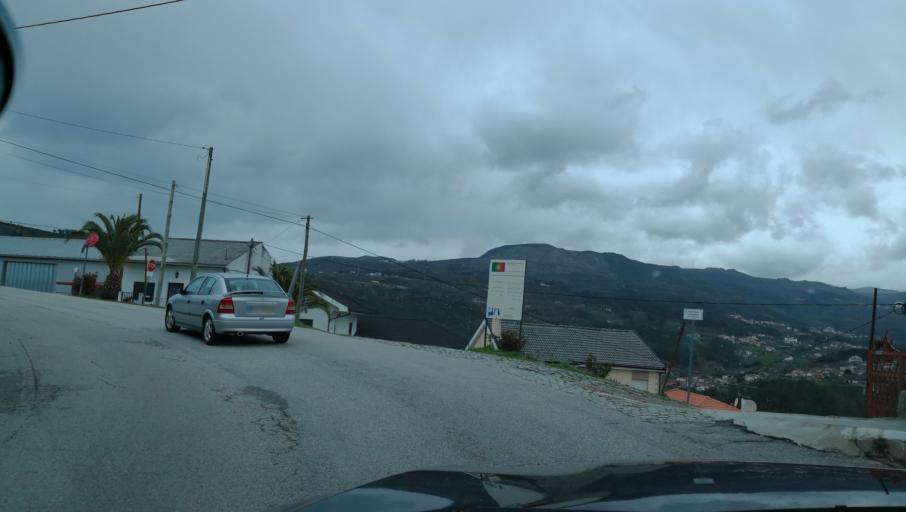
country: PT
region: Vila Real
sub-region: Vila Real
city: Vila Real
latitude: 41.2786
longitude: -7.7796
